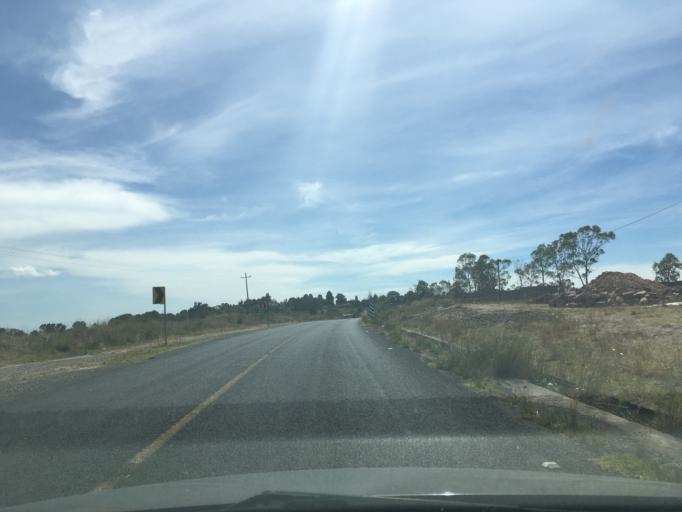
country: MX
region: Queretaro
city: Amealco
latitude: 20.2104
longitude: -100.1228
